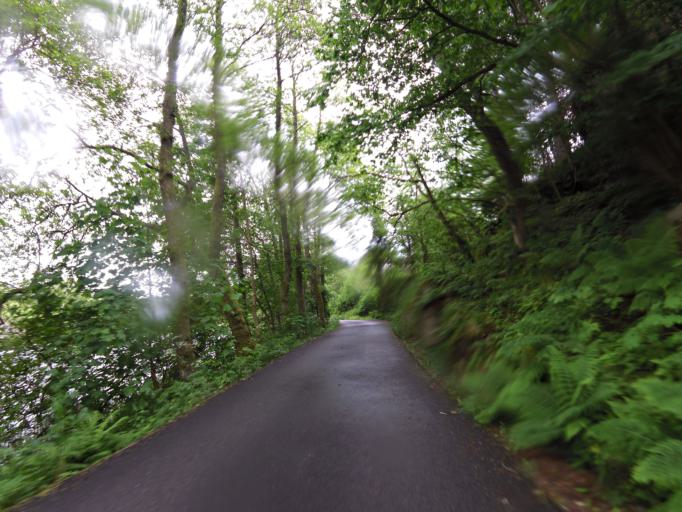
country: NO
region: Vest-Agder
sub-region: Mandal
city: Mandal
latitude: 58.0112
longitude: 7.5253
